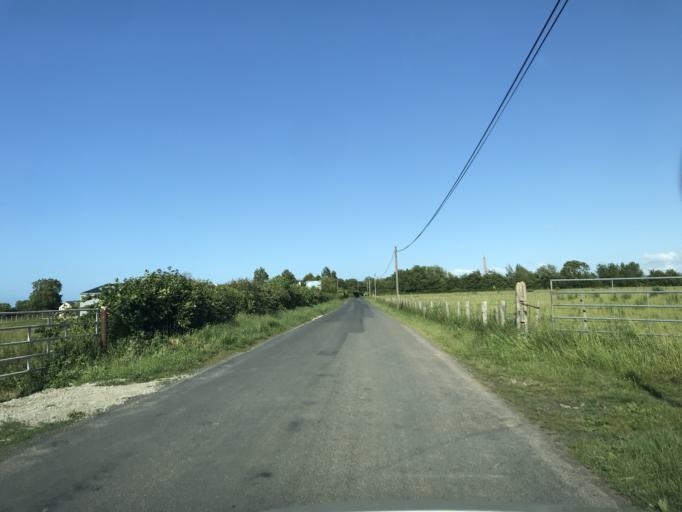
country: FR
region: Lower Normandy
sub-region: Departement du Calvados
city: Grandcamp-Maisy
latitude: 49.3811
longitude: -1.0644
